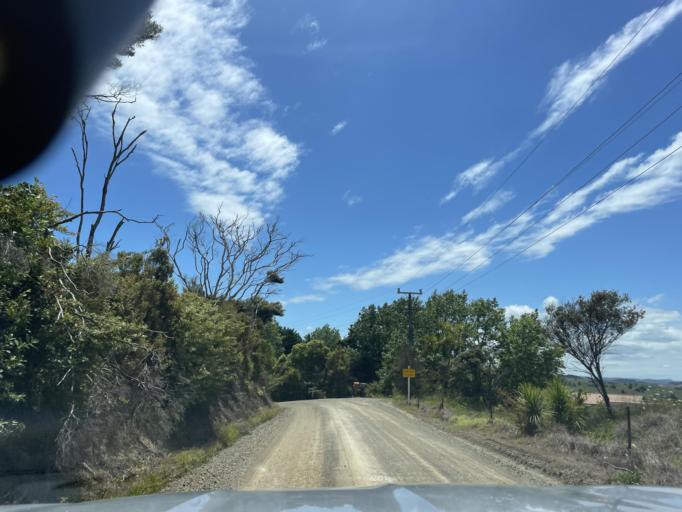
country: NZ
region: Auckland
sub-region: Auckland
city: Wellsford
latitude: -36.2199
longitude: 174.3603
